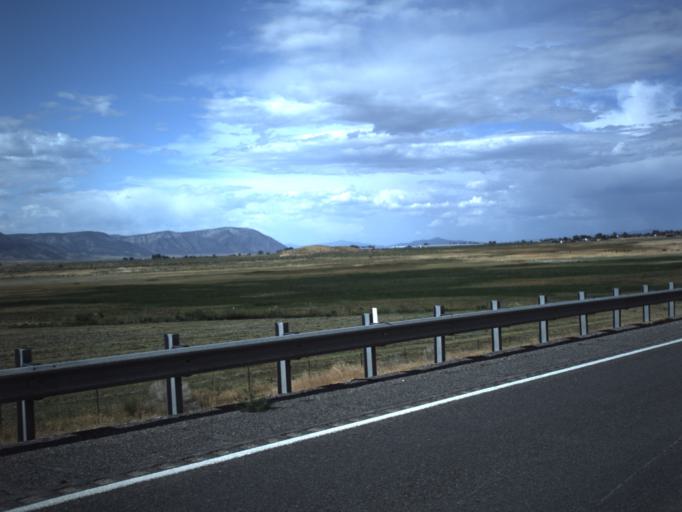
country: US
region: Utah
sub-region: Sanpete County
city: Manti
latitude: 39.2317
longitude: -111.6663
